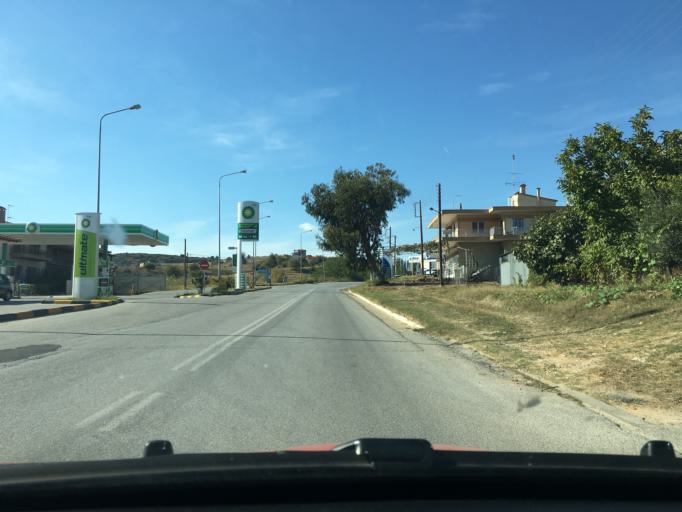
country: GR
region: Central Macedonia
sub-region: Nomos Chalkidikis
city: Nea Roda
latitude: 40.3790
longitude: 23.9226
